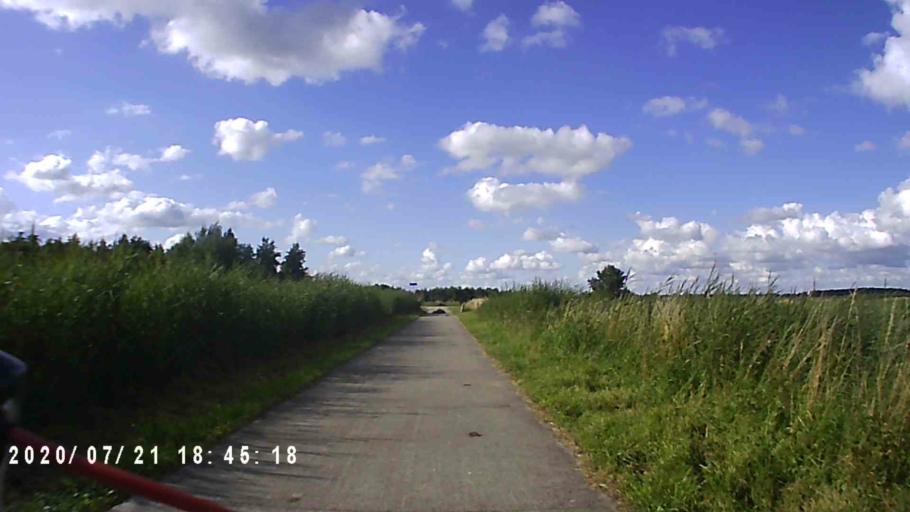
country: NL
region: Groningen
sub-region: Gemeente Hoogezand-Sappemeer
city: Hoogezand
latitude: 53.2089
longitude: 6.7493
